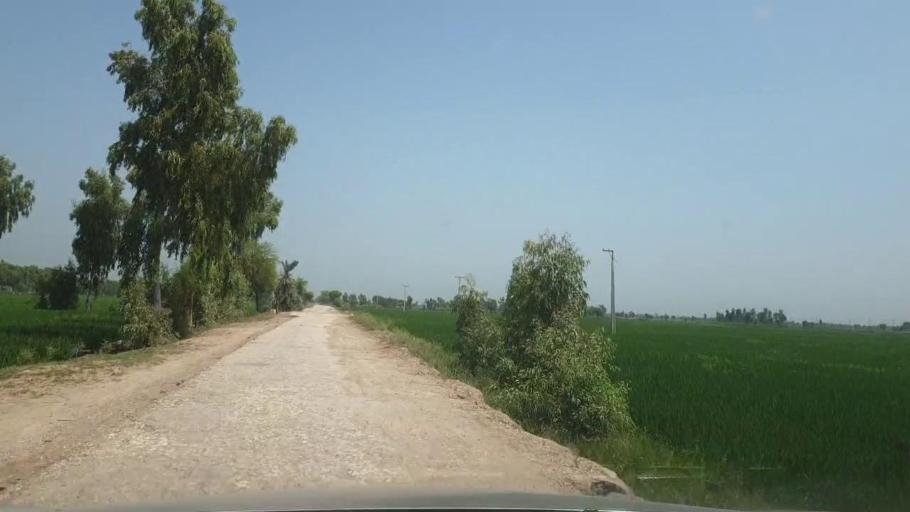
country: PK
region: Sindh
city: Warah
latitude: 27.5091
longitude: 67.7601
